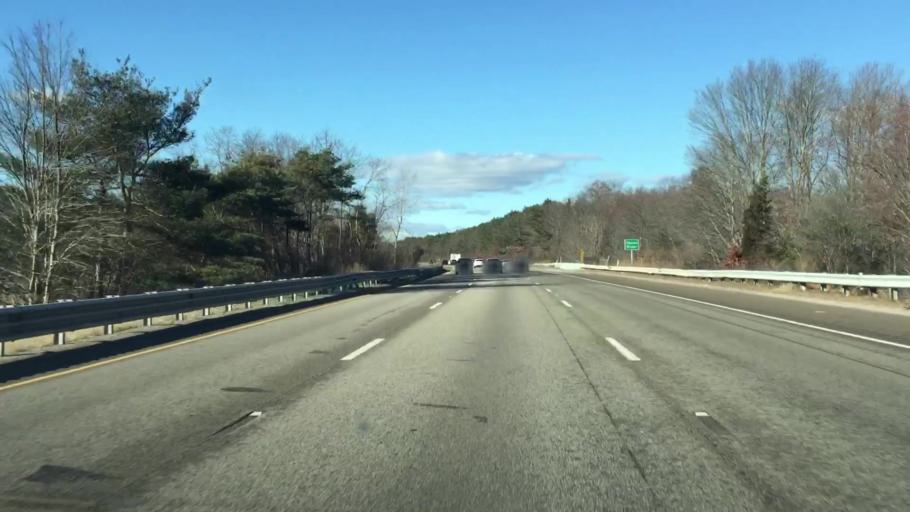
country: US
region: Massachusetts
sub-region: Bristol County
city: Norton Center
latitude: 41.9868
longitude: -71.1643
